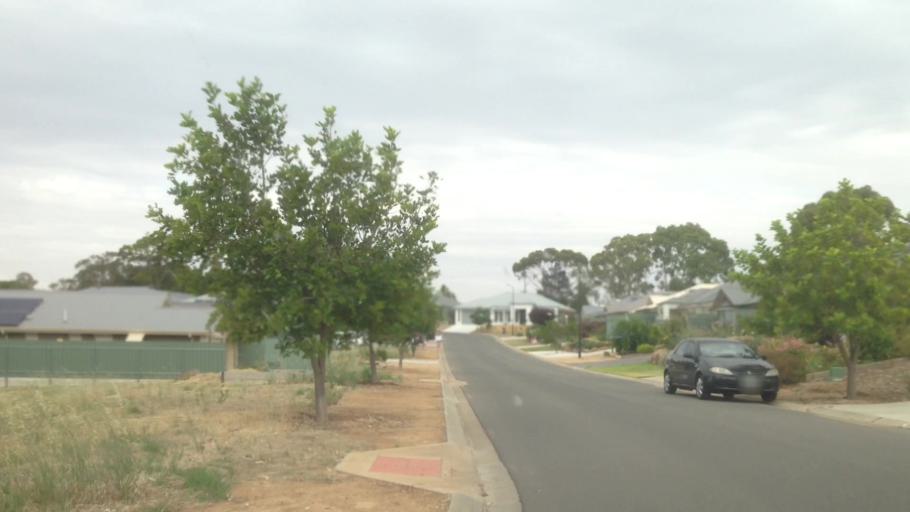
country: AU
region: South Australia
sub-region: Barossa
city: Williamstown
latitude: -34.6721
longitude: 138.8862
